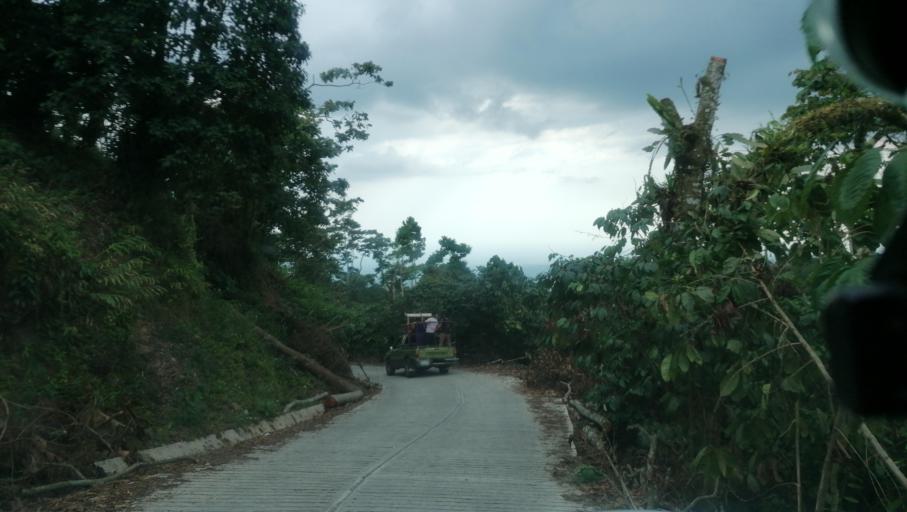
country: MX
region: Chiapas
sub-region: Cacahoatan
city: Benito Juarez
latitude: 15.0744
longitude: -92.1618
